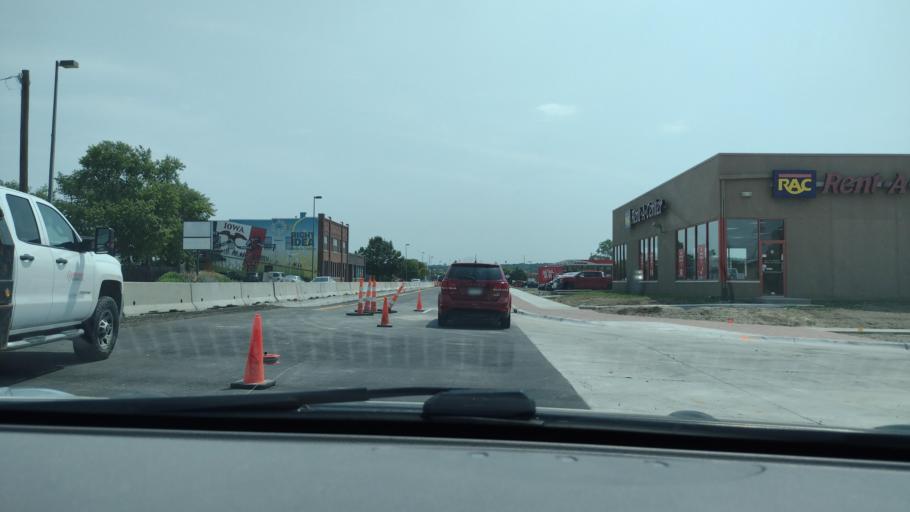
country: US
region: Iowa
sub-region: Pottawattamie County
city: Council Bluffs
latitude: 41.2618
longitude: -95.8723
